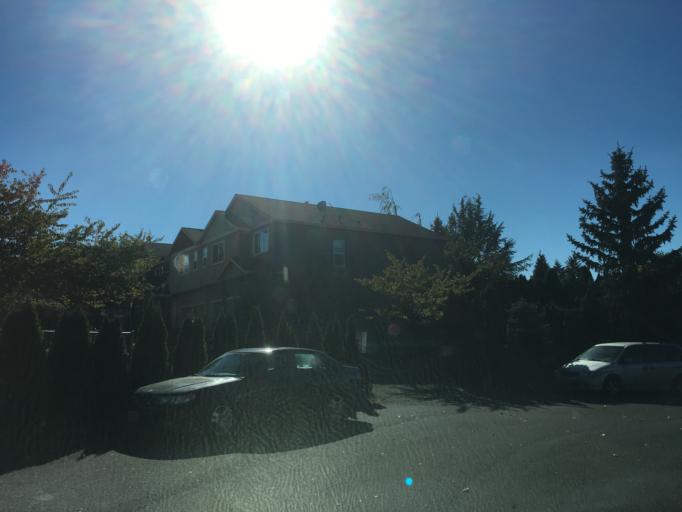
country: US
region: Oregon
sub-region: Multnomah County
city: Gresham
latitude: 45.4838
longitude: -122.3947
